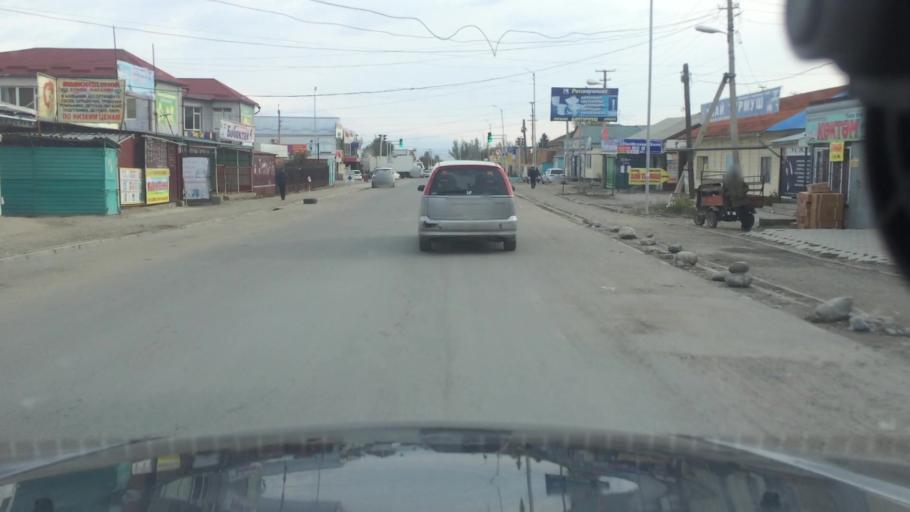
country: KG
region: Ysyk-Koel
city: Karakol
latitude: 42.4924
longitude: 78.3859
